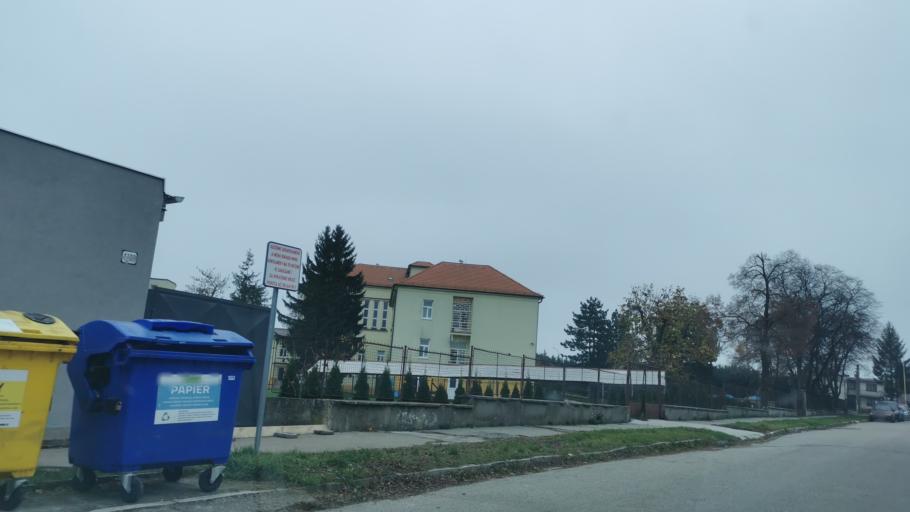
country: SK
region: Trnavsky
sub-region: Okres Skalica
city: Holic
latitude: 48.8200
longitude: 17.1619
